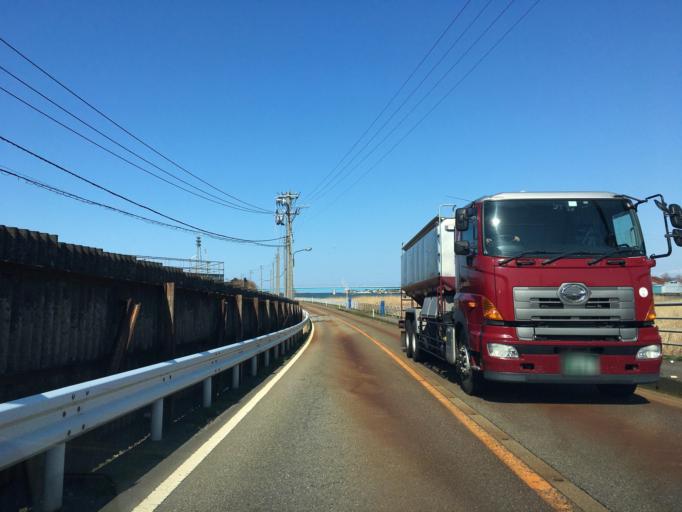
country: JP
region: Toyama
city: Nishishinminato
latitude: 36.7822
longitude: 137.0493
